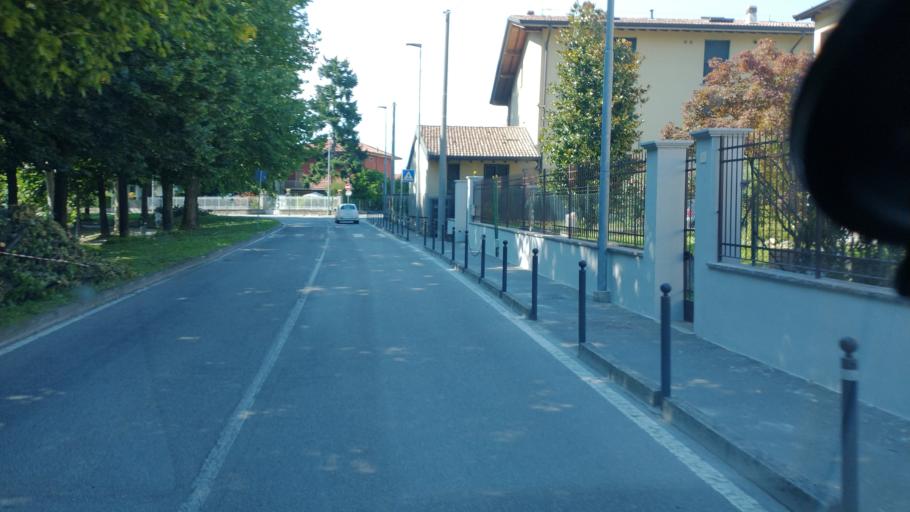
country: IT
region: Lombardy
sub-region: Provincia di Bergamo
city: Cologno al Serio
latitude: 45.5806
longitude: 9.7108
